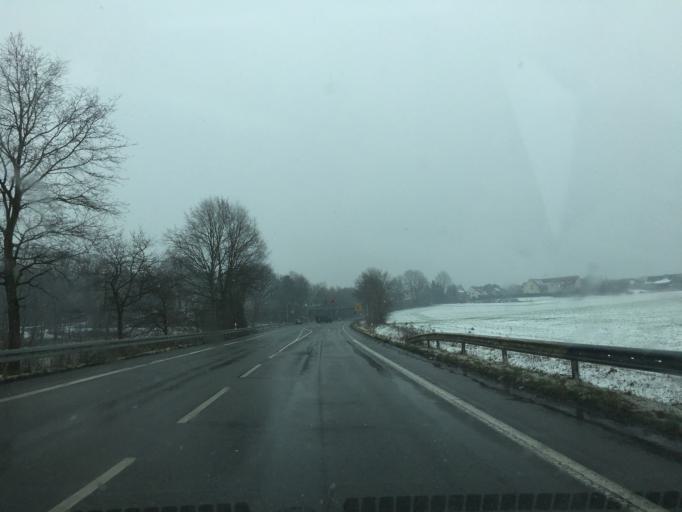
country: DE
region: North Rhine-Westphalia
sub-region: Regierungsbezirk Munster
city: Klein Reken
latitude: 51.8027
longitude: 7.0354
